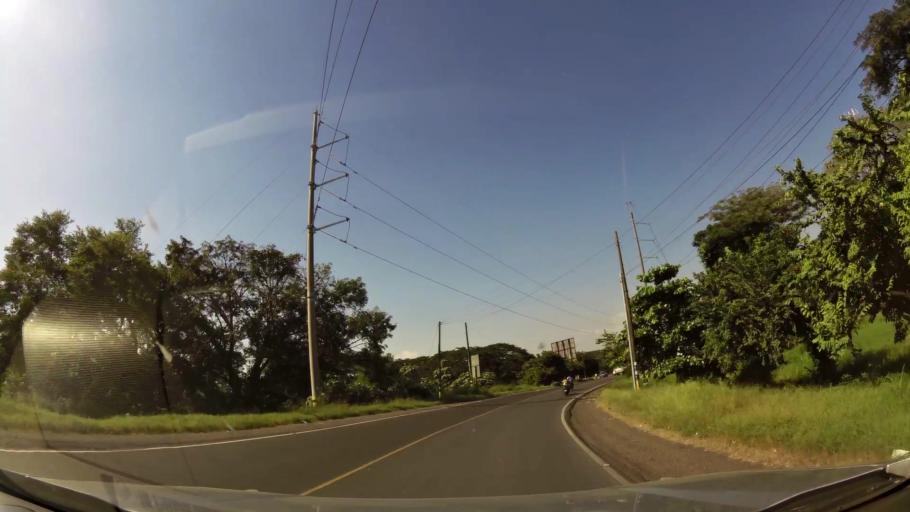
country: GT
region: Escuintla
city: Puerto San Jose
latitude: 13.9331
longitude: -90.7855
